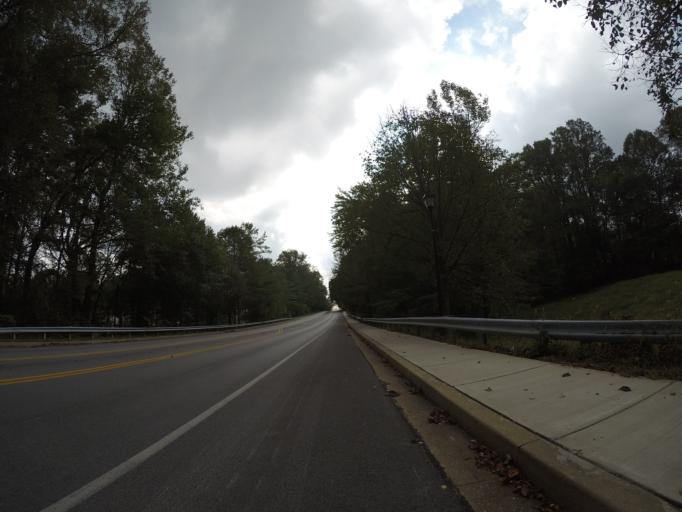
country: US
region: Maryland
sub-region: Howard County
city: Columbia
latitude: 39.2632
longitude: -76.8625
